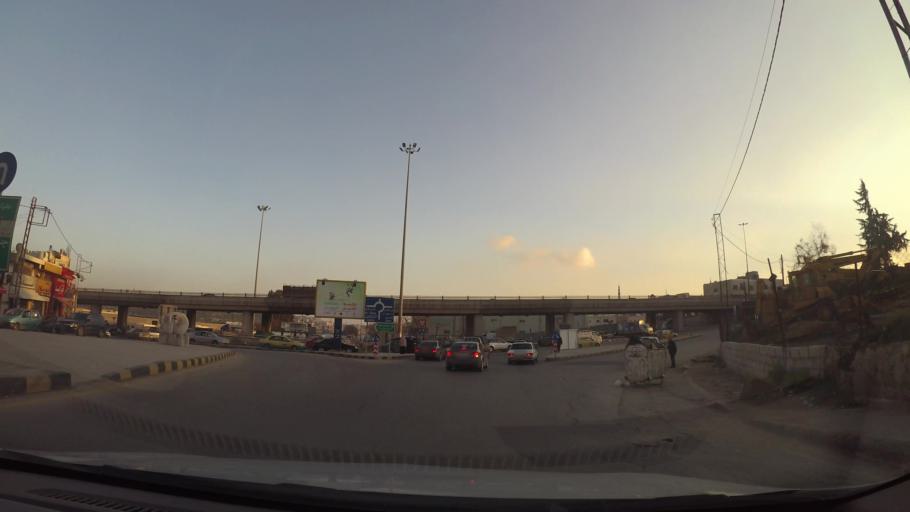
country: JO
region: Amman
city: Al Quwaysimah
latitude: 31.9014
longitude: 35.9376
